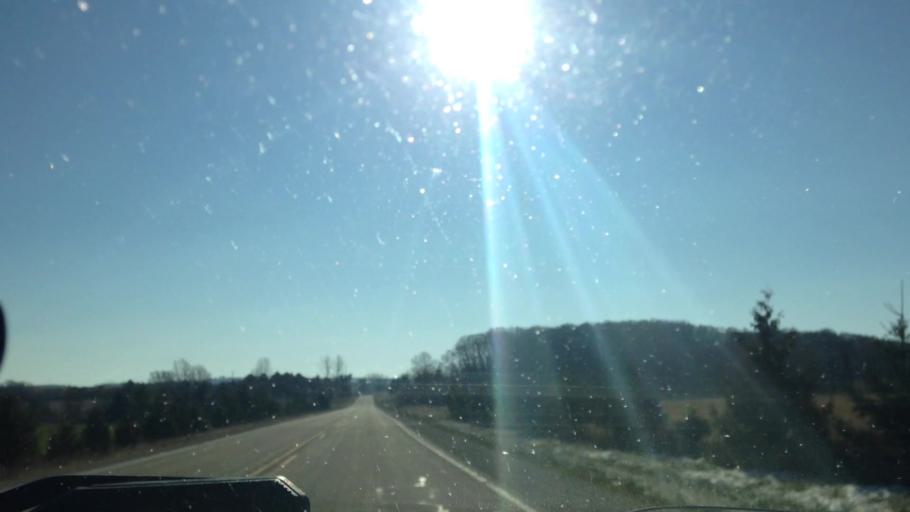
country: US
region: Wisconsin
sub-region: Dodge County
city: Mayville
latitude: 43.4842
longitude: -88.5111
